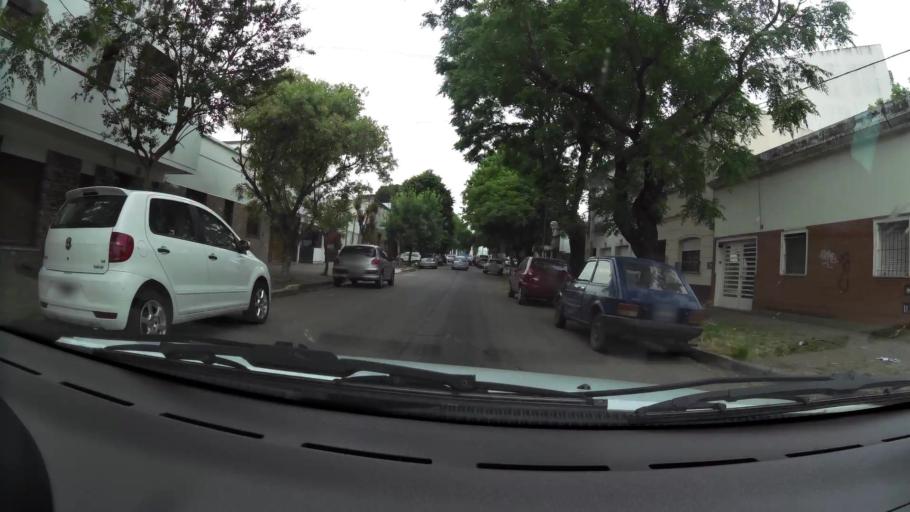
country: AR
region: Buenos Aires
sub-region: Partido de La Plata
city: La Plata
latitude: -34.9323
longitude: -57.9558
